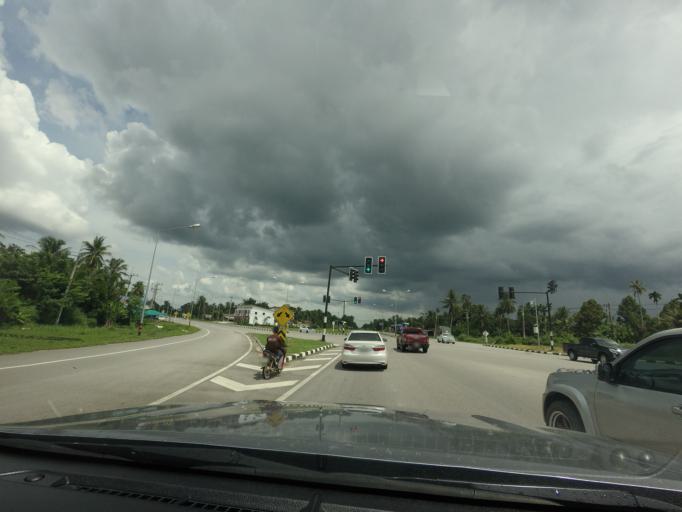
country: TH
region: Chumphon
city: Chumphon
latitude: 10.5517
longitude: 99.1644
